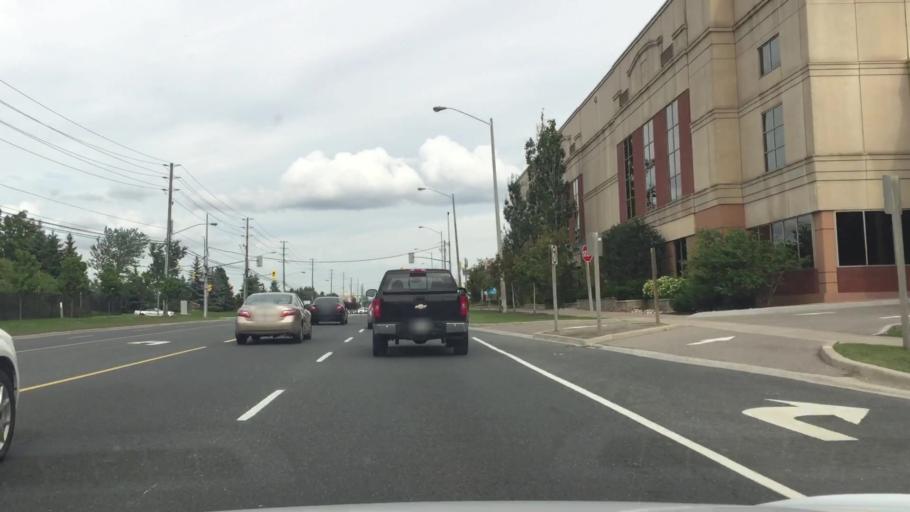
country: CA
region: Ontario
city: Vaughan
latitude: 43.8321
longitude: -79.5279
